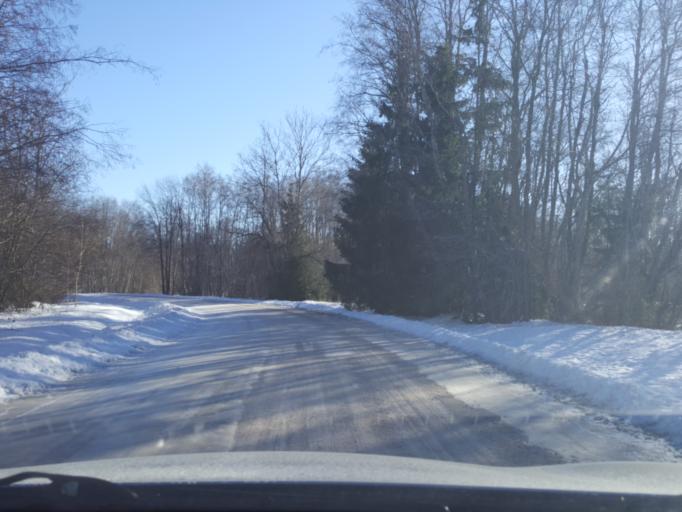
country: EE
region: Viljandimaa
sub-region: Viljandi linn
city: Viljandi
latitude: 58.4618
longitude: 25.5539
